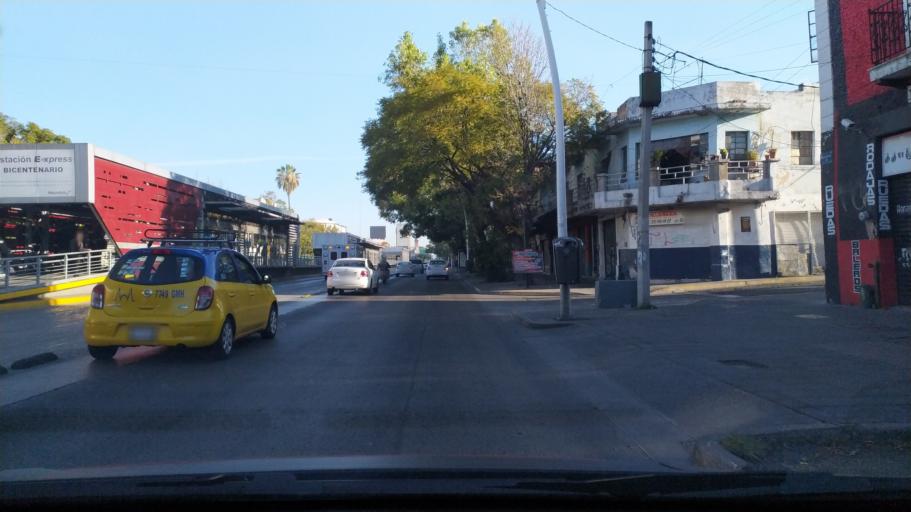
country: MX
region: Jalisco
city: Guadalajara
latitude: 20.6684
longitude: -103.3454
